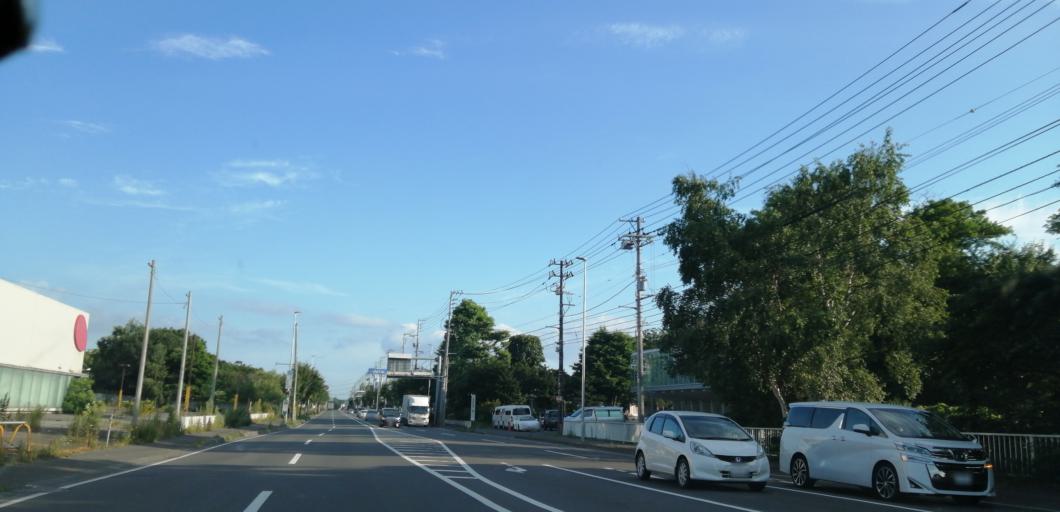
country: JP
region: Hokkaido
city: Kitahiroshima
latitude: 42.9973
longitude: 141.5620
